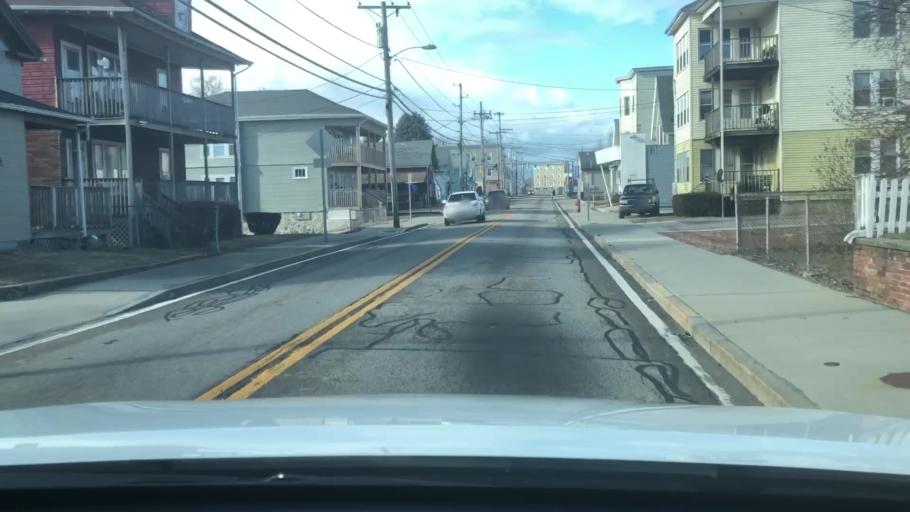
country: US
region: Rhode Island
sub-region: Providence County
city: Woonsocket
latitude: 42.0155
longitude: -71.4962
